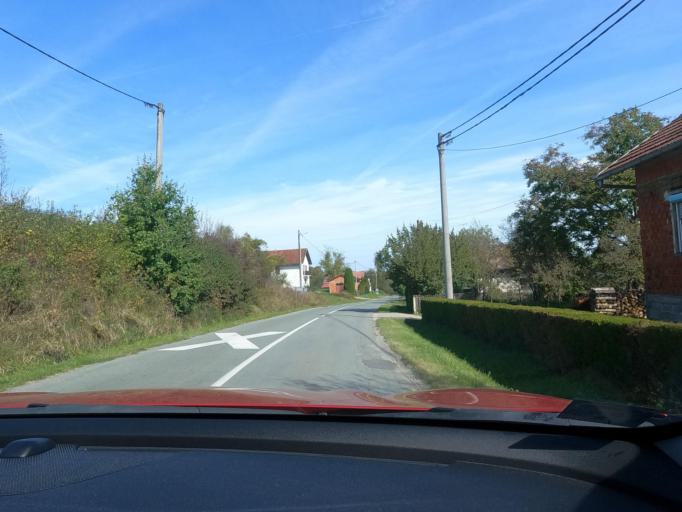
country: HR
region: Sisacko-Moslavacka
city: Petrinja
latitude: 45.4000
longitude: 16.2881
